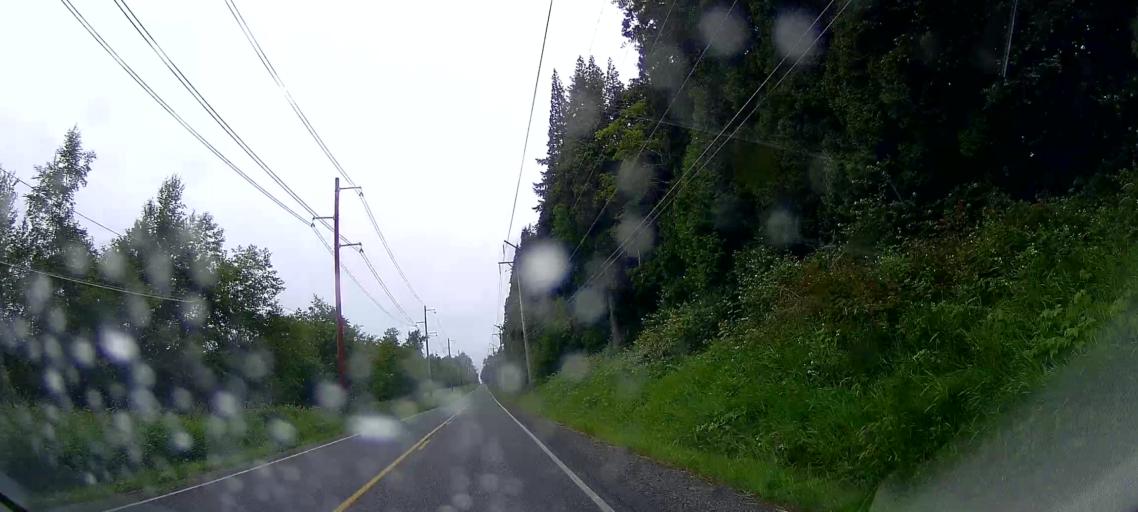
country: US
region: Washington
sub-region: Whatcom County
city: Birch Bay
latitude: 48.8708
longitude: -122.7037
